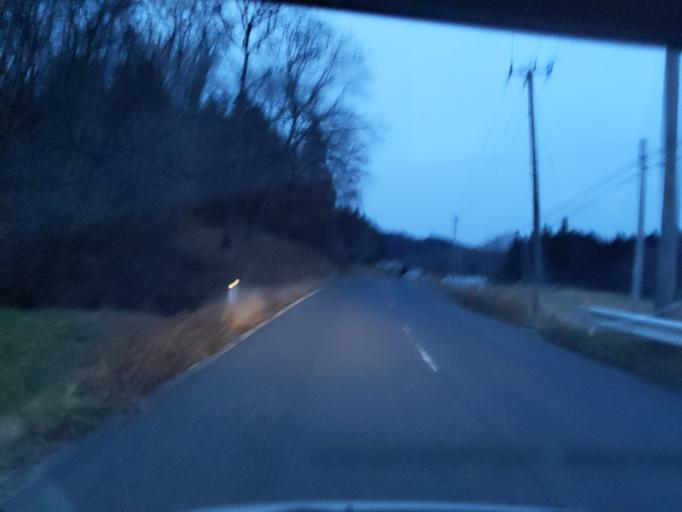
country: JP
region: Iwate
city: Ichinoseki
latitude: 38.8298
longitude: 141.1193
